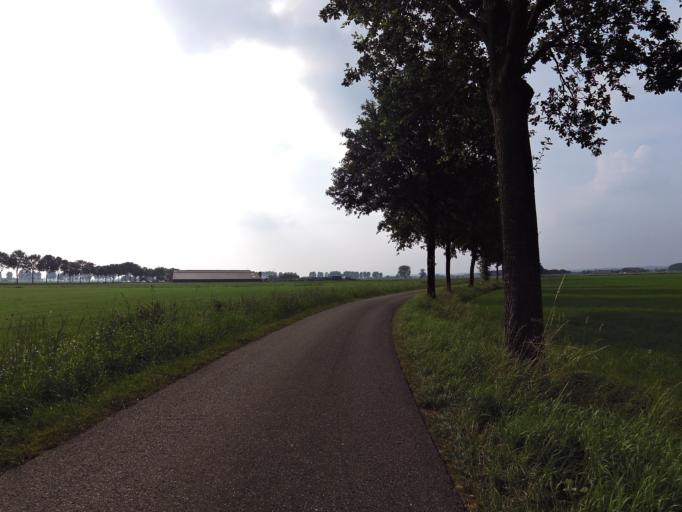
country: NL
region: Gelderland
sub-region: Gemeente Zevenaar
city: Zevenaar
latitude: 51.9678
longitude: 6.0739
